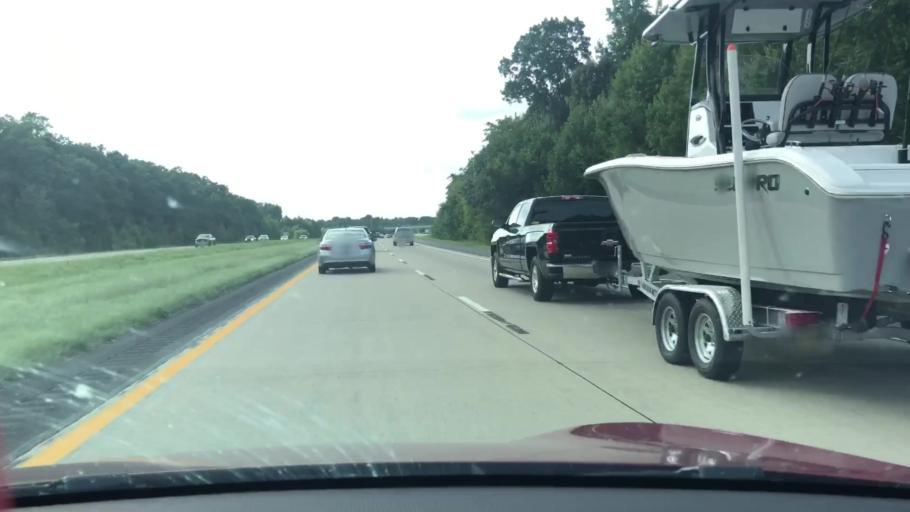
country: US
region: Delaware
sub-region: Kent County
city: Cheswold
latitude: 39.2221
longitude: -75.5655
